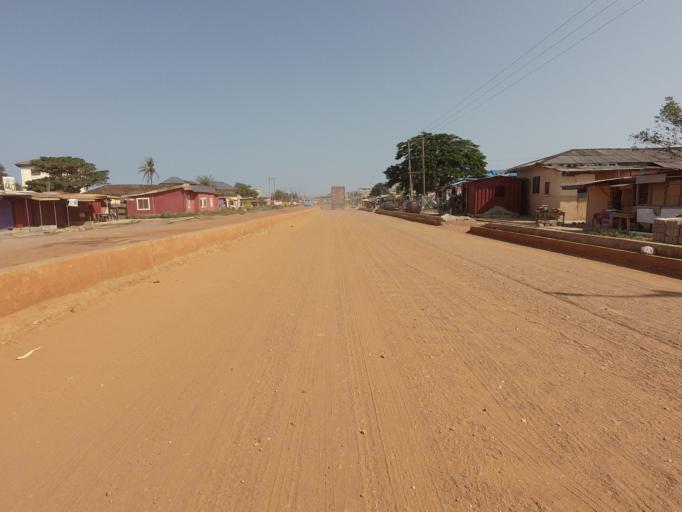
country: GH
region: Greater Accra
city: Teshi Old Town
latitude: 5.5812
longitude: -0.1128
